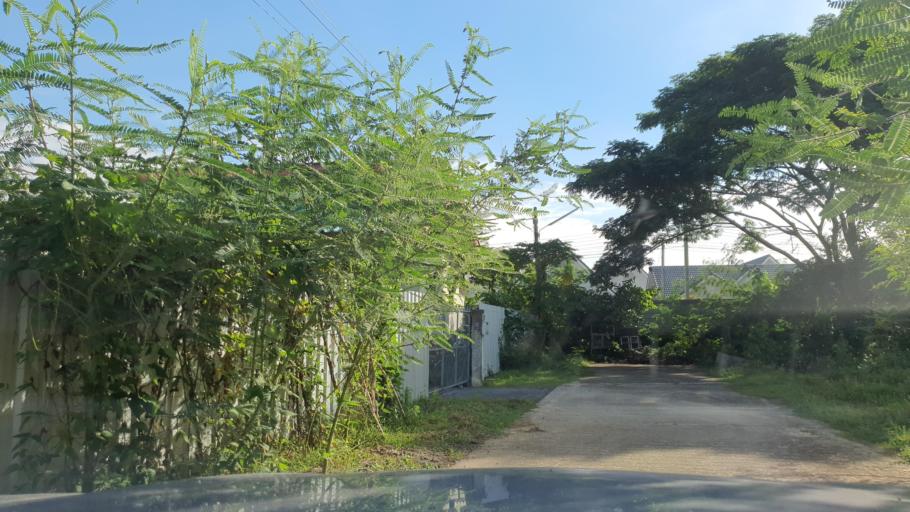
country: TH
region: Chiang Mai
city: San Kamphaeng
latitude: 18.7492
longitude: 99.1044
